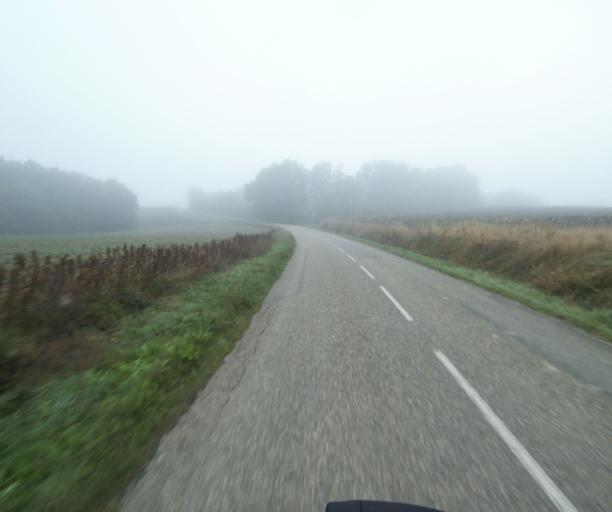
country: FR
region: Midi-Pyrenees
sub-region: Departement du Tarn-et-Garonne
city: Orgueil
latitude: 43.9363
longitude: 1.4194
